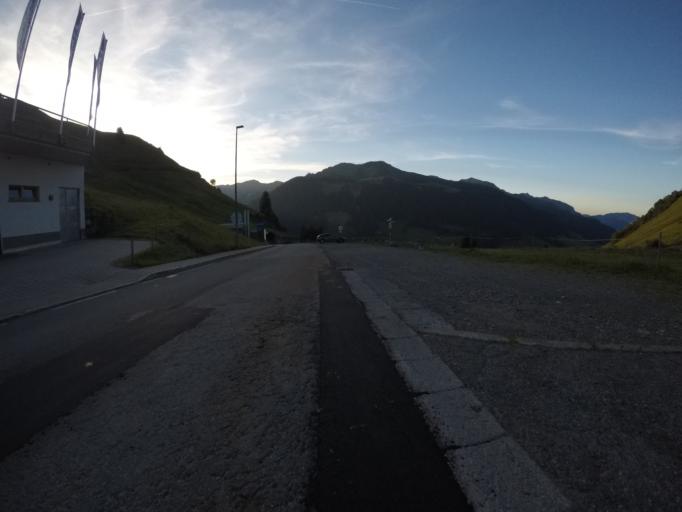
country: AT
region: Vorarlberg
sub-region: Politischer Bezirk Bregenz
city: Damuels
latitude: 47.2728
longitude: 9.9071
